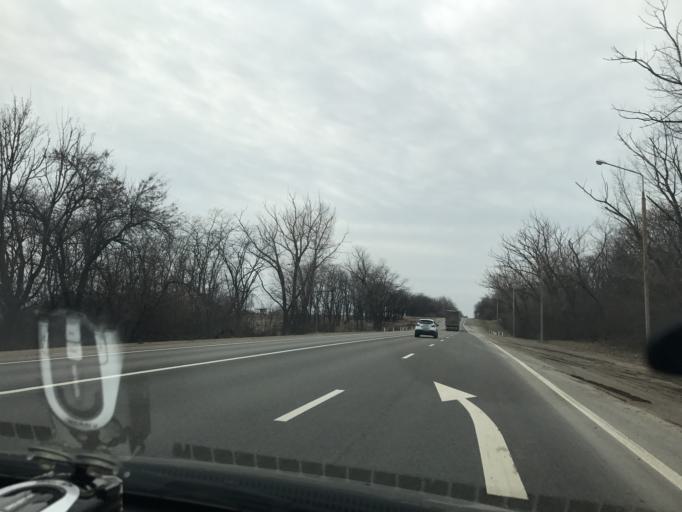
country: RU
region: Krasnodarskiy
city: Mirskoy
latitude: 45.6707
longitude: 40.3253
